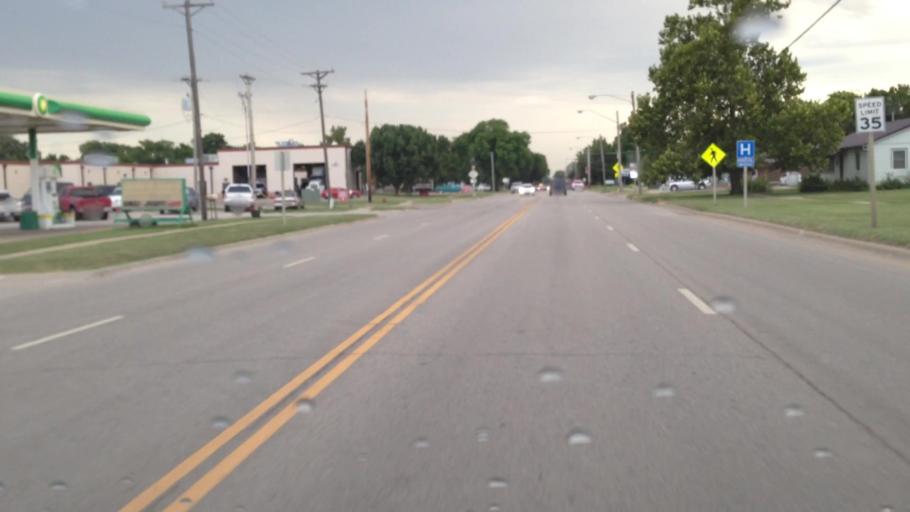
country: US
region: Kansas
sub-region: Coffey County
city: Burlington
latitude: 38.2037
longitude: -95.7386
